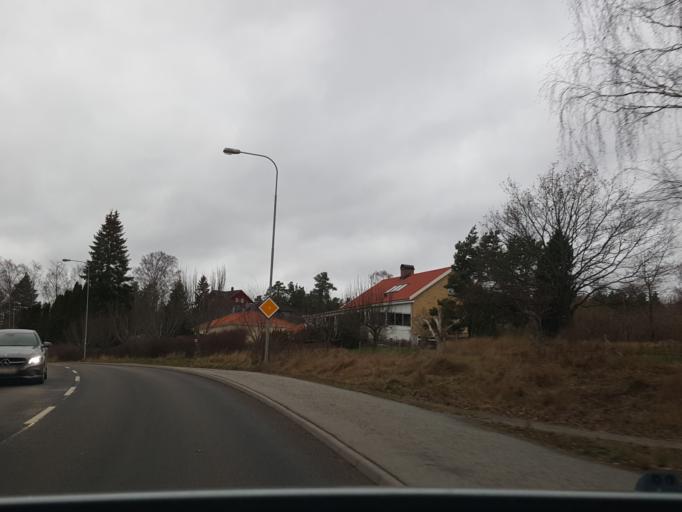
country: SE
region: Stockholm
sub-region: Nacka Kommun
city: Boo
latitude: 59.3294
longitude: 18.2814
